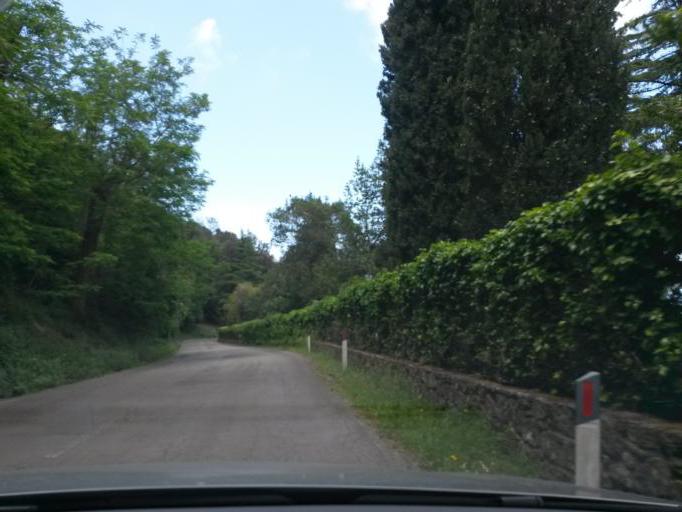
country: IT
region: Tuscany
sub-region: Provincia di Livorno
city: Marciana Marina
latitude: 42.7878
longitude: 10.1868
